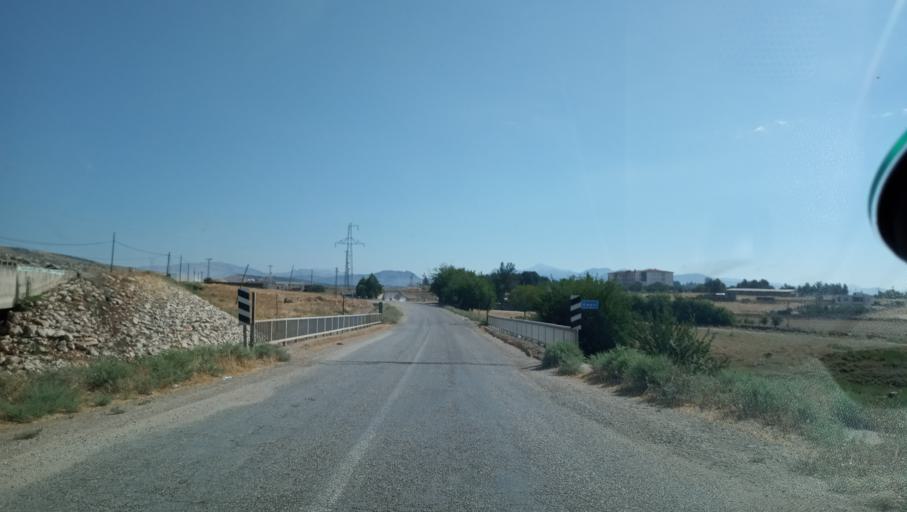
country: TR
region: Diyarbakir
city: Malabadi
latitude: 38.1350
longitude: 41.1891
